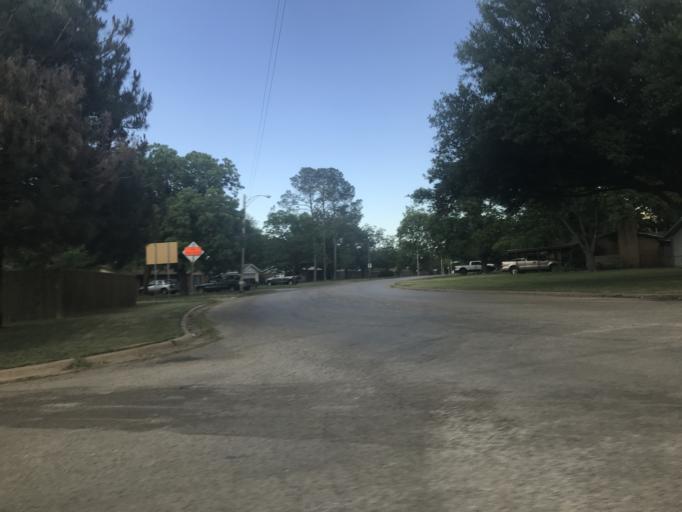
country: US
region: Texas
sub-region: Taylor County
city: Abilene
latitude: 32.4252
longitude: -99.7663
